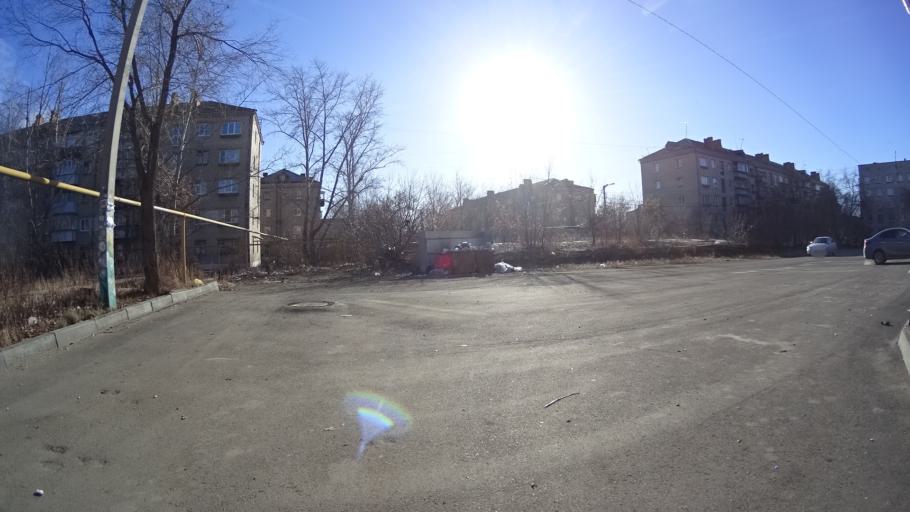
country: RU
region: Chelyabinsk
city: Troitsk
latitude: 54.0795
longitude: 61.5331
